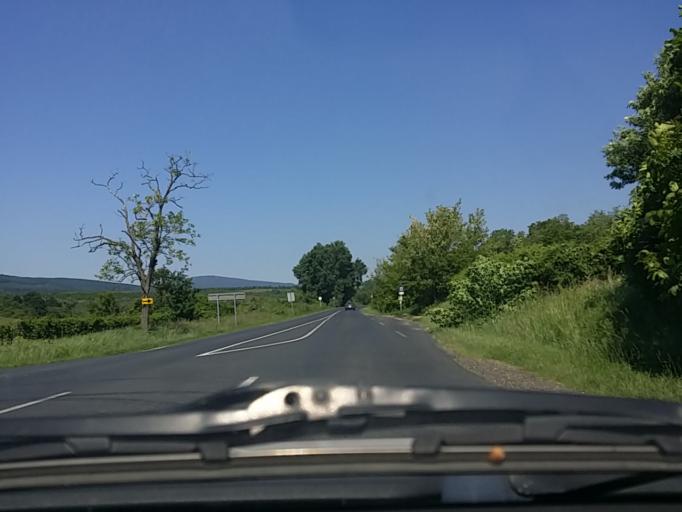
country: HU
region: Pest
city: Csobanka
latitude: 47.6561
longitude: 18.9781
